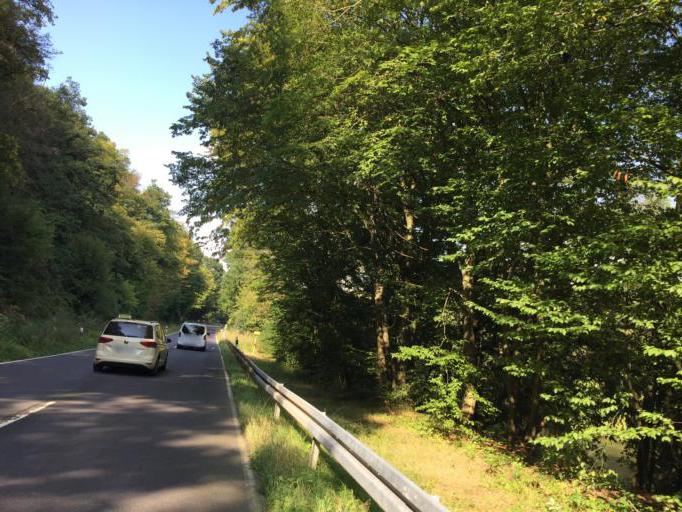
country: DE
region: Hesse
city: Lollar
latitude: 50.6537
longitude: 8.6868
